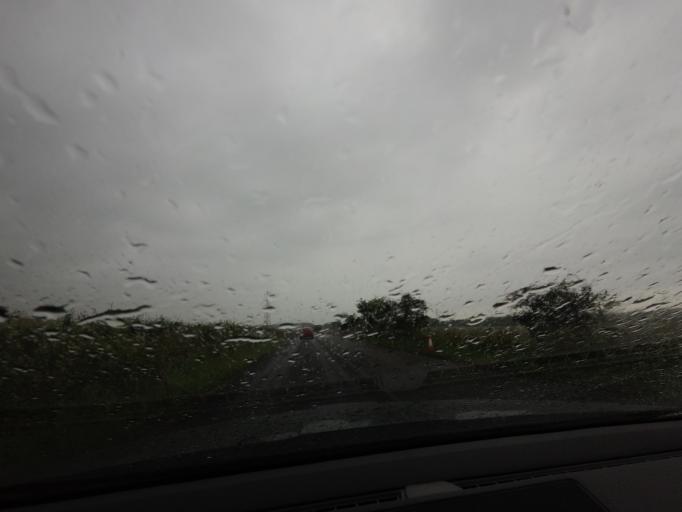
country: GB
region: Scotland
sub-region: Aberdeenshire
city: Mintlaw
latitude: 57.6121
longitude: -1.9498
